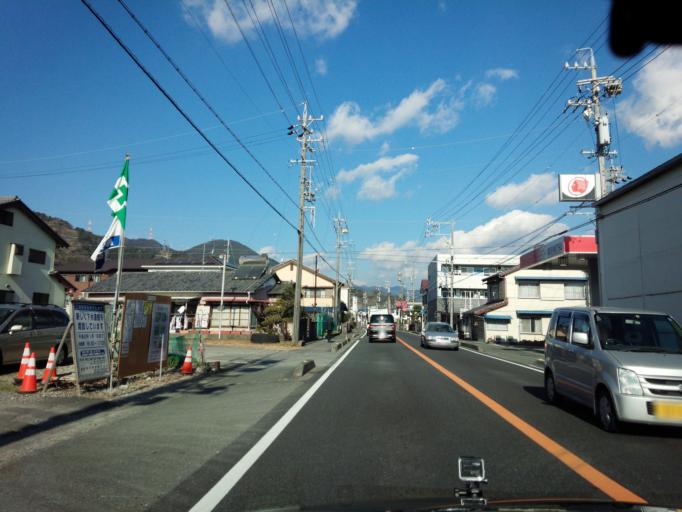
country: JP
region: Shizuoka
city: Shizuoka-shi
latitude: 35.0660
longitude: 138.5235
